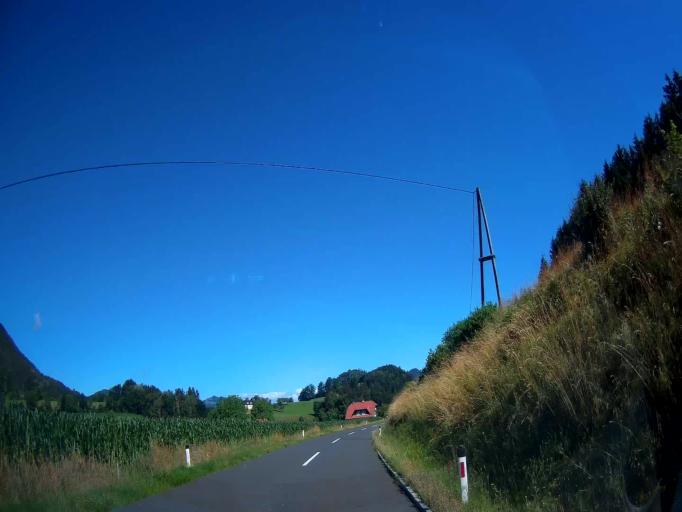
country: AT
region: Carinthia
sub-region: Politischer Bezirk Volkermarkt
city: Voelkermarkt
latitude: 46.6794
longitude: 14.5775
